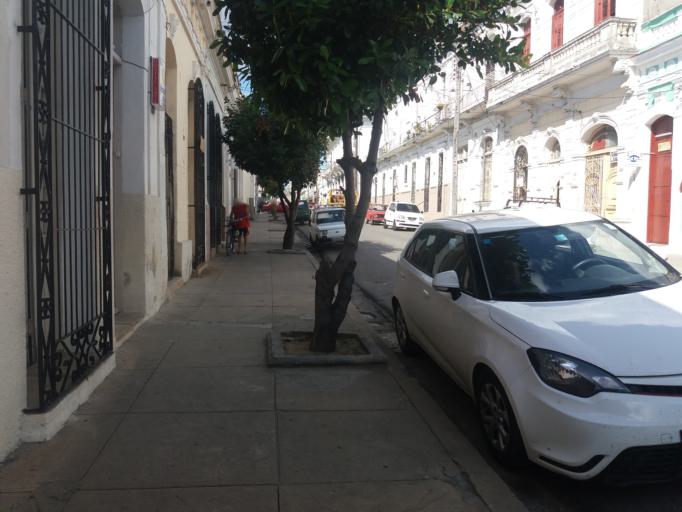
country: CU
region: Cienfuegos
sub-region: Municipio de Cienfuegos
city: Cienfuegos
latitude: 22.1436
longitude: -80.4496
